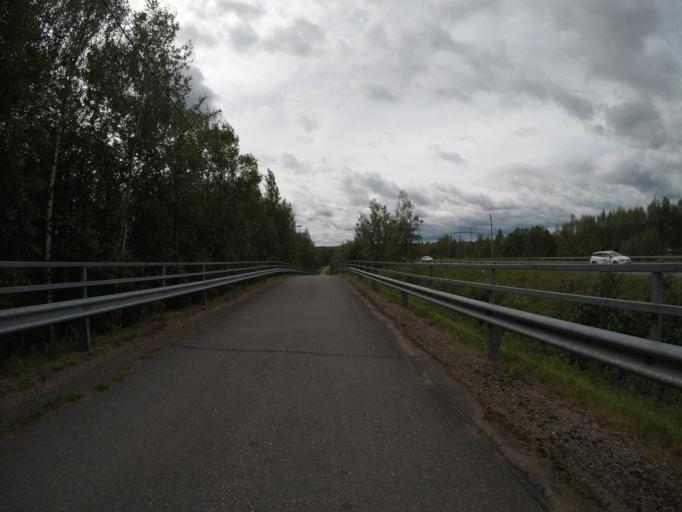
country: FI
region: Haeme
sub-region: Haemeenlinna
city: Haemeenlinna
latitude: 60.9806
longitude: 24.5026
